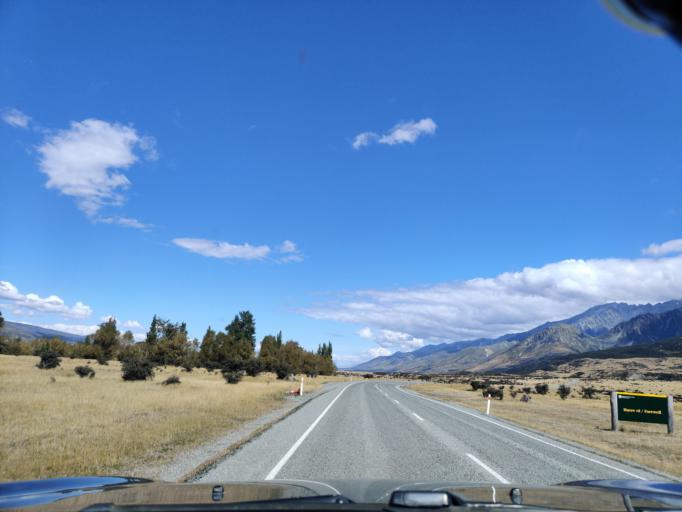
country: NZ
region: Canterbury
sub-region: Timaru District
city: Pleasant Point
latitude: -43.7886
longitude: 170.1196
